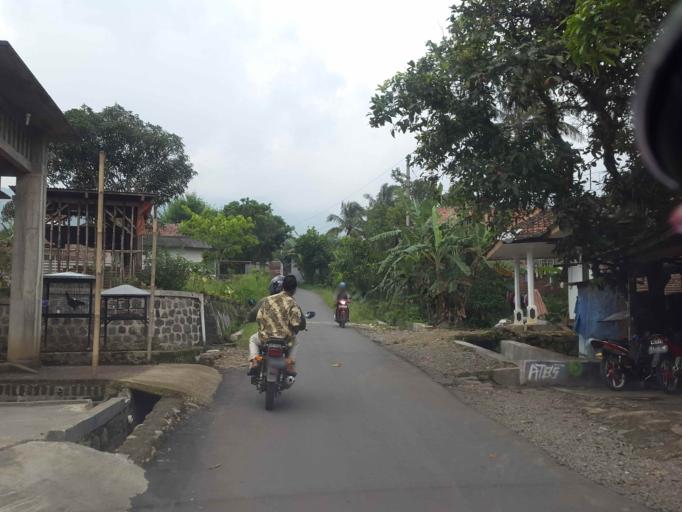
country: ID
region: Central Java
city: Muara
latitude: -7.2822
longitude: 109.0421
